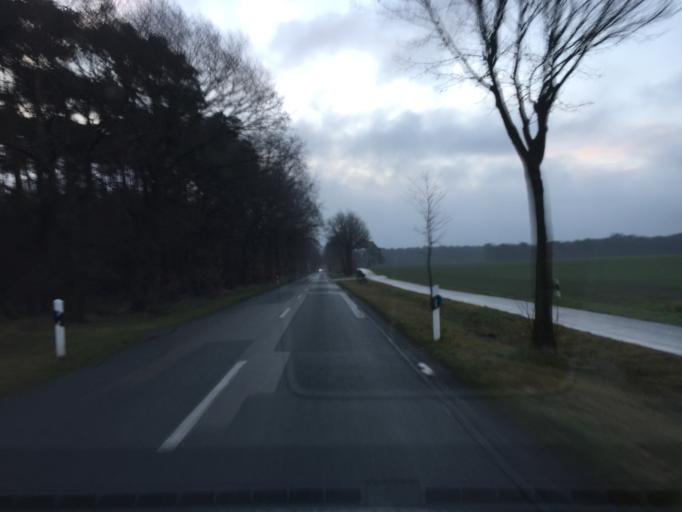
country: DE
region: Lower Saxony
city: Liebenau
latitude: 52.6209
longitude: 9.0617
